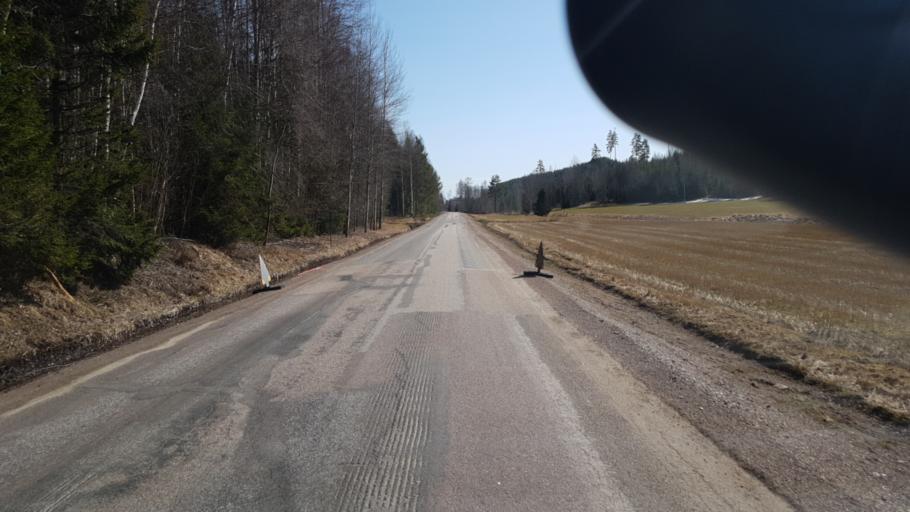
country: SE
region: Vaermland
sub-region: Arvika Kommun
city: Arvika
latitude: 59.6656
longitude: 12.7973
